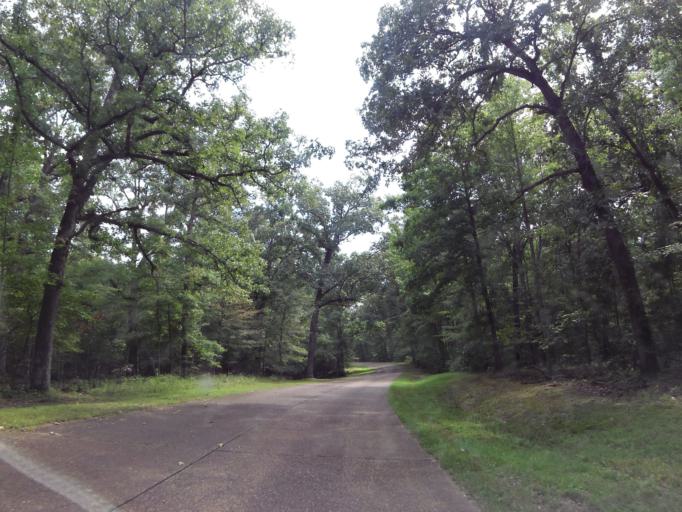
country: US
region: Tennessee
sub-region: Hardin County
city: Crump
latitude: 35.1233
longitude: -88.3564
